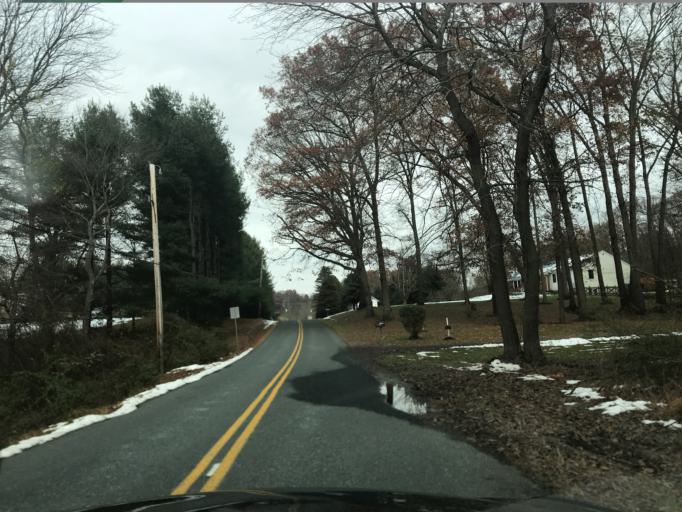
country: US
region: Pennsylvania
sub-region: York County
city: Susquehanna Trails
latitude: 39.6882
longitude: -76.4200
